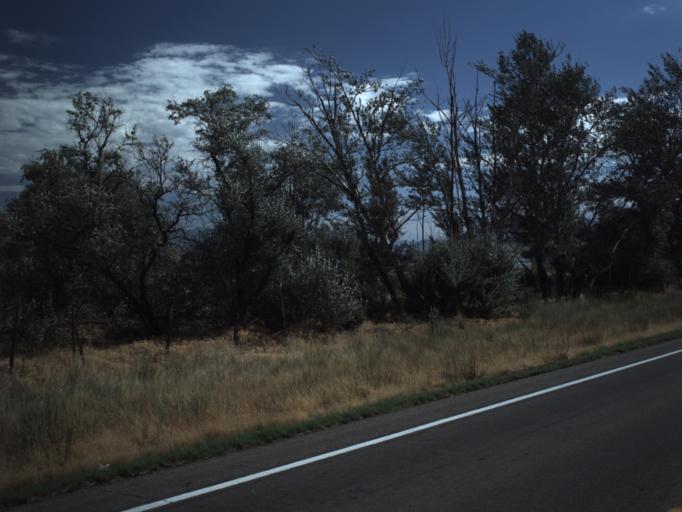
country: US
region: Utah
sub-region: Utah County
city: Genola
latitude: 39.9525
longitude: -111.9180
